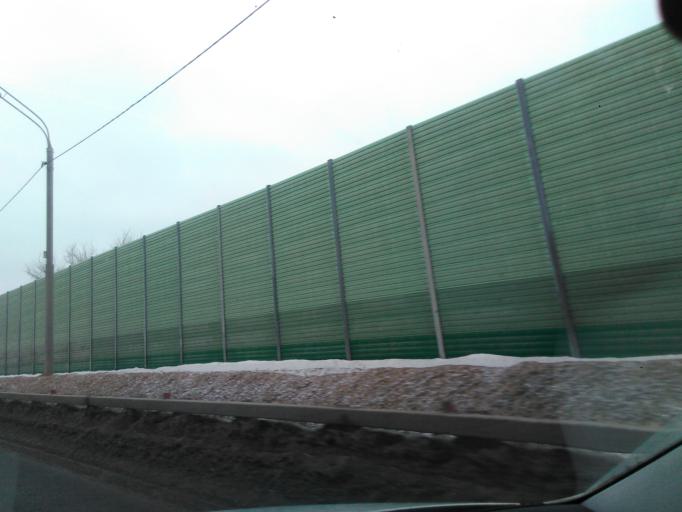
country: RU
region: Moskovskaya
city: Yermolino
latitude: 56.1285
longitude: 37.5115
